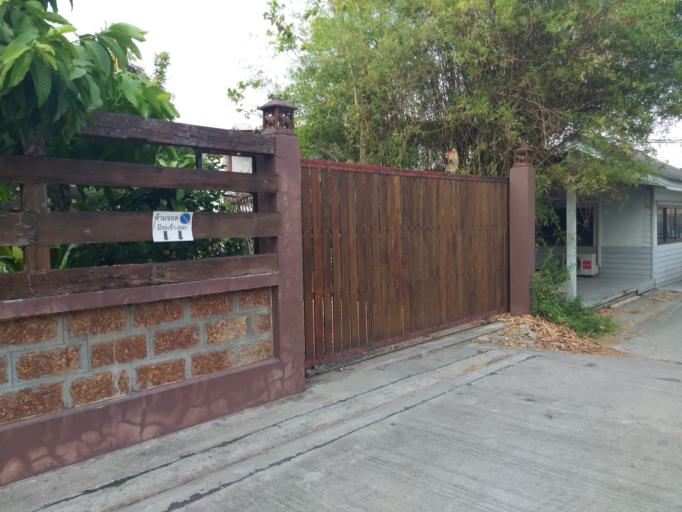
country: TH
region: Bangkok
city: Lat Phrao
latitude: 13.8231
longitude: 100.6161
